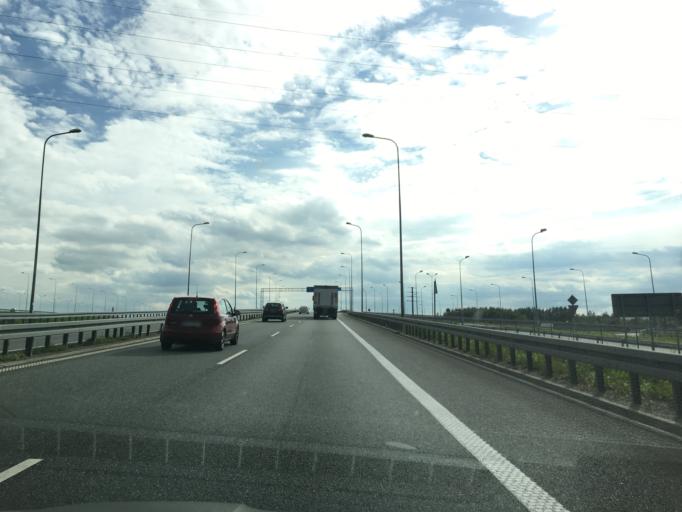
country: PL
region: Silesian Voivodeship
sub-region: Powiat gliwicki
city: Przyszowice
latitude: 50.2650
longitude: 18.7233
